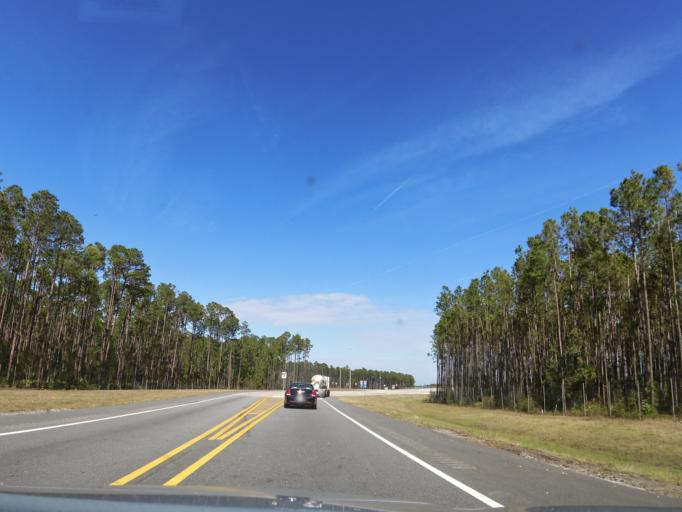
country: US
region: Georgia
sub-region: McIntosh County
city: Darien
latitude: 31.3030
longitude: -81.4833
